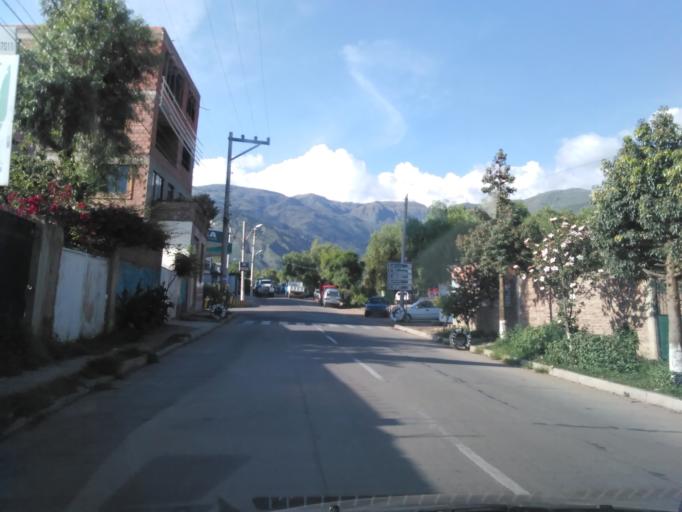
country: BO
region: Cochabamba
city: Cochabamba
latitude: -17.3399
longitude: -66.2142
